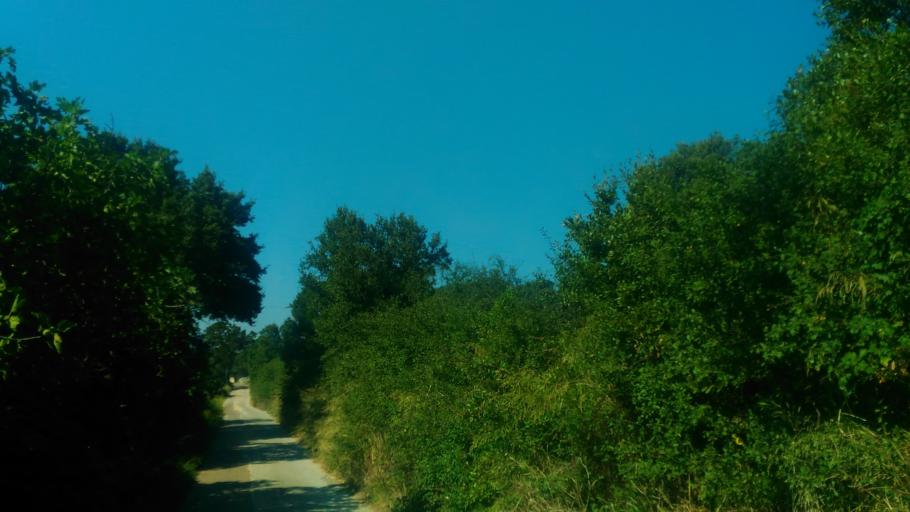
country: IT
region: Apulia
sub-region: Provincia di Bari
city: Noci
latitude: 40.8135
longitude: 17.1796
